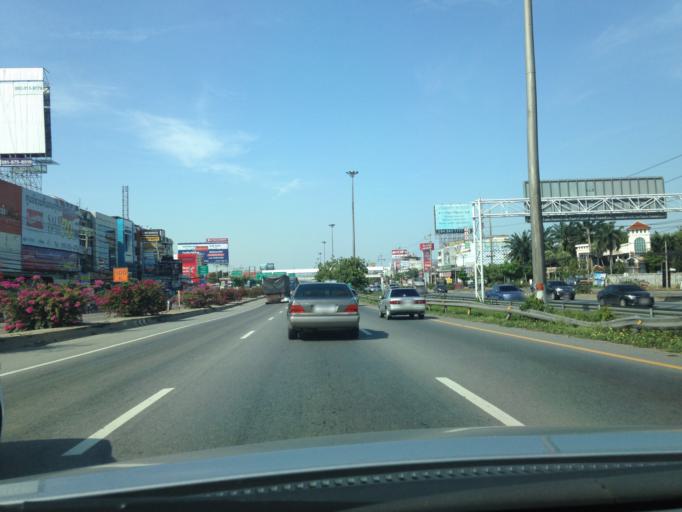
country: TH
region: Nonthaburi
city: Bang Yai
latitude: 13.8530
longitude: 100.4119
